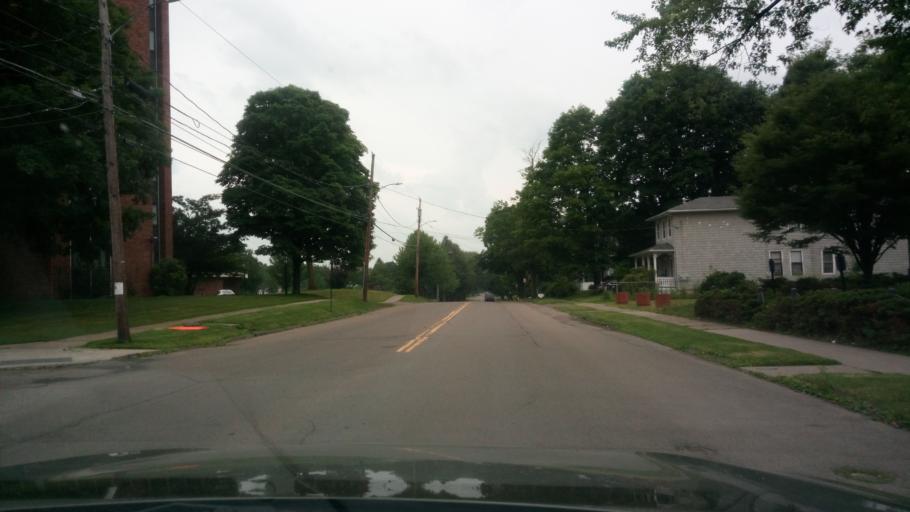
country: US
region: New York
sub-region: Chemung County
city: Elmira
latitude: 42.0966
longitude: -76.8188
